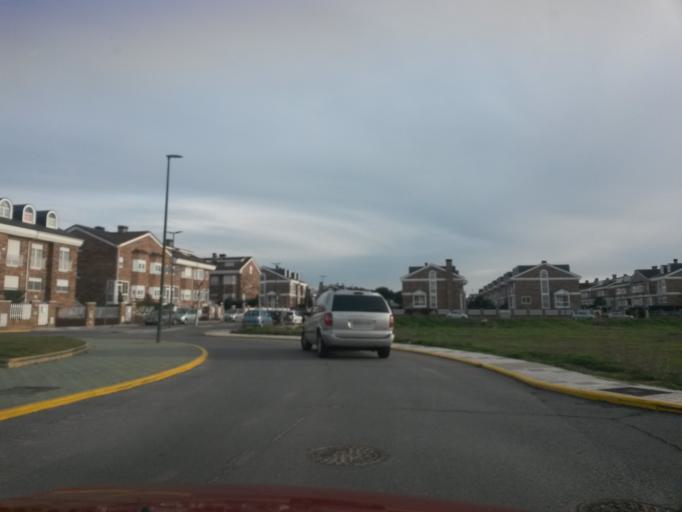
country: ES
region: Castille and Leon
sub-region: Provincia de Salamanca
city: Santa Marta de Tormes
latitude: 40.9549
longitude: -5.6449
